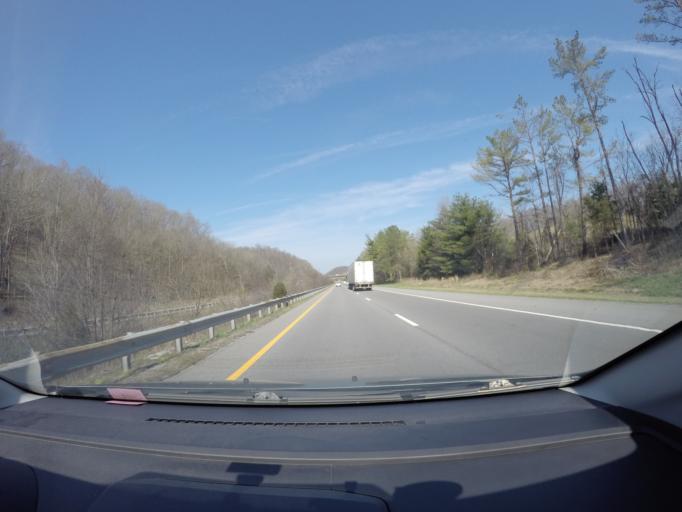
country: US
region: Tennessee
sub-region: Coffee County
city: New Union
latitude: 35.5566
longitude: -86.2008
